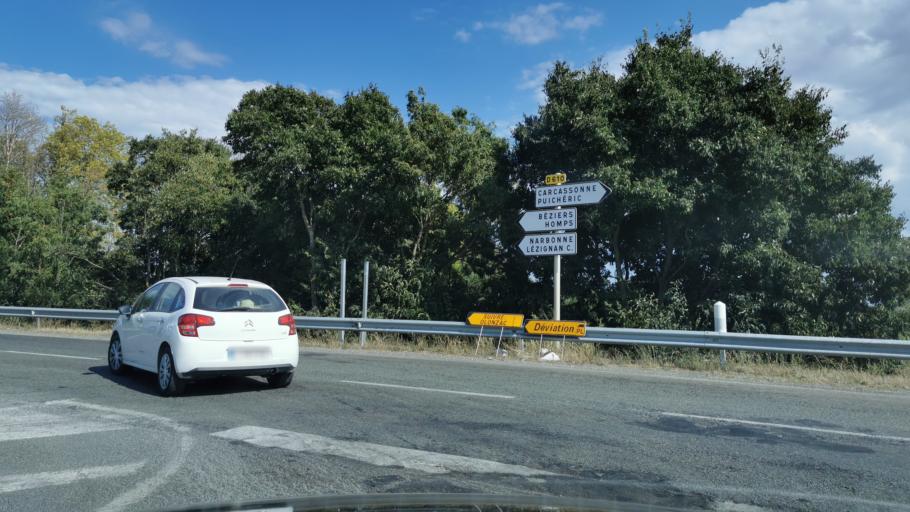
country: FR
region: Languedoc-Roussillon
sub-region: Departement de l'Aude
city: Azille
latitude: 43.2495
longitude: 2.6725
